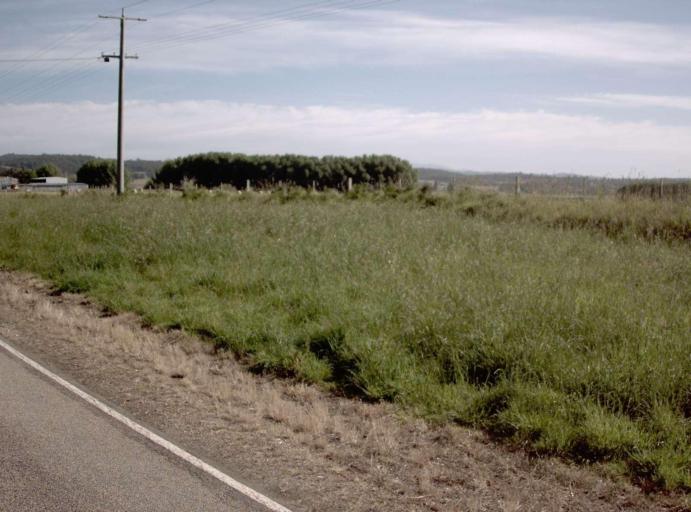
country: AU
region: Victoria
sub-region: East Gippsland
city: Bairnsdale
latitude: -37.7316
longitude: 147.8106
